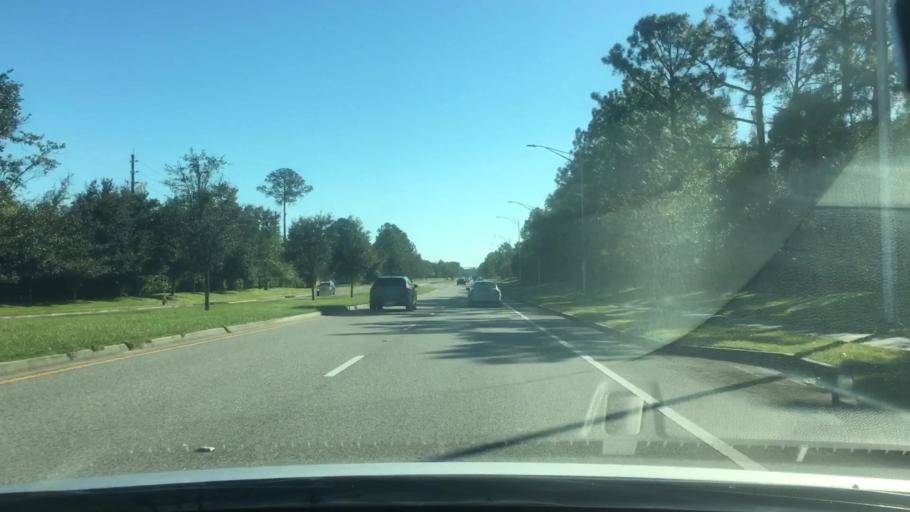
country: US
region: Florida
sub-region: Duval County
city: Neptune Beach
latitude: 30.3053
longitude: -81.4593
